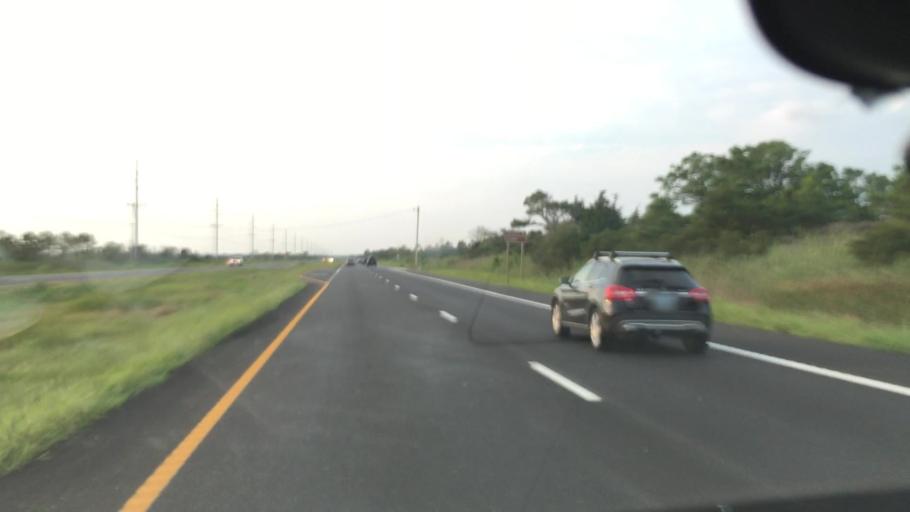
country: US
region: Delaware
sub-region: Sussex County
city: Rehoboth Beach
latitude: 38.6621
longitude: -75.0700
